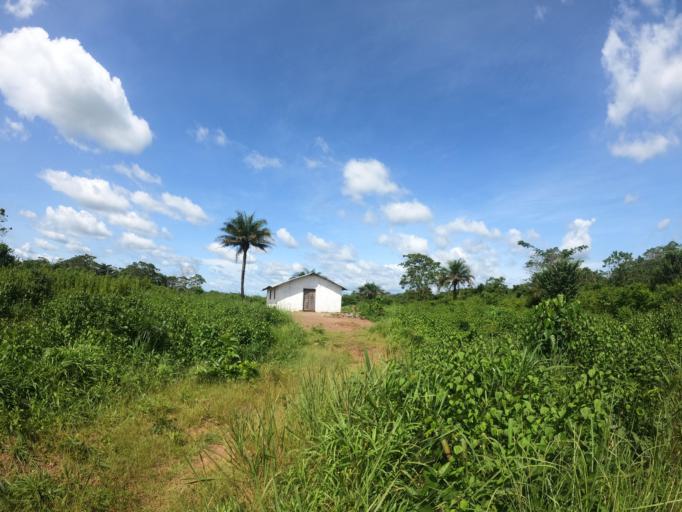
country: SL
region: Northern Province
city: Masingbi
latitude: 8.8304
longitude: -11.9908
